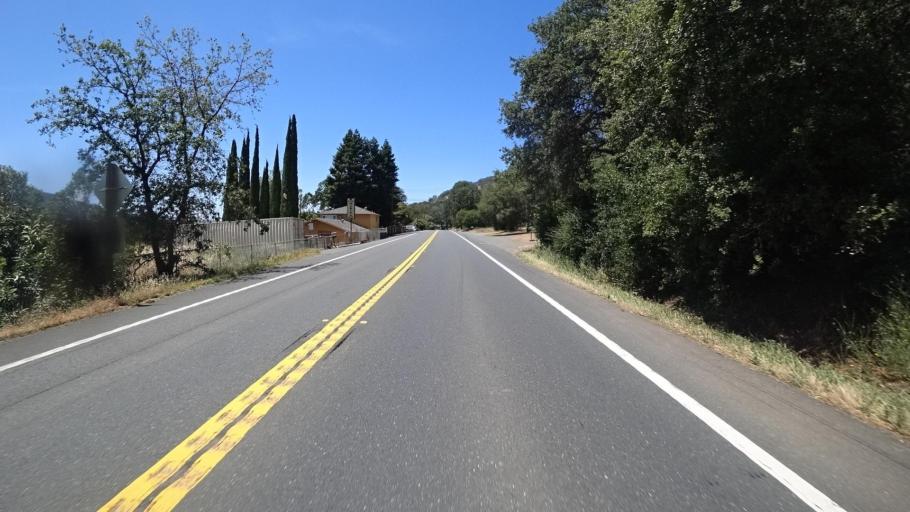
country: US
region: California
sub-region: Lake County
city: Clearlake Oaks
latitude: 39.0232
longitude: -122.7186
